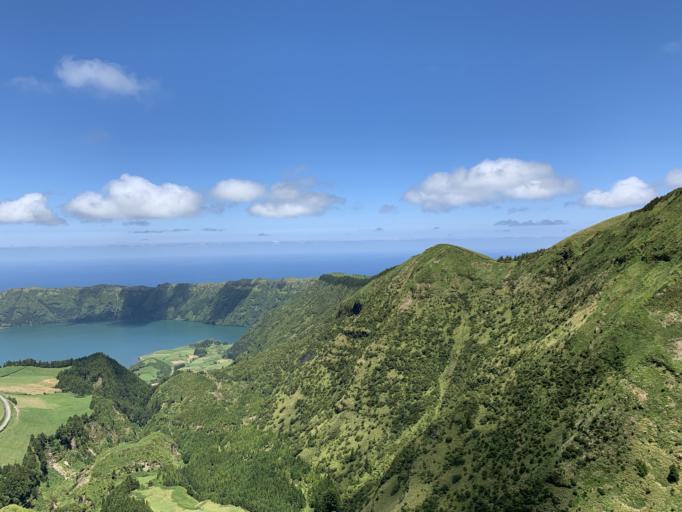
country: PT
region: Azores
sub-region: Ponta Delgada
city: Arrifes
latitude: 37.8423
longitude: -25.7621
